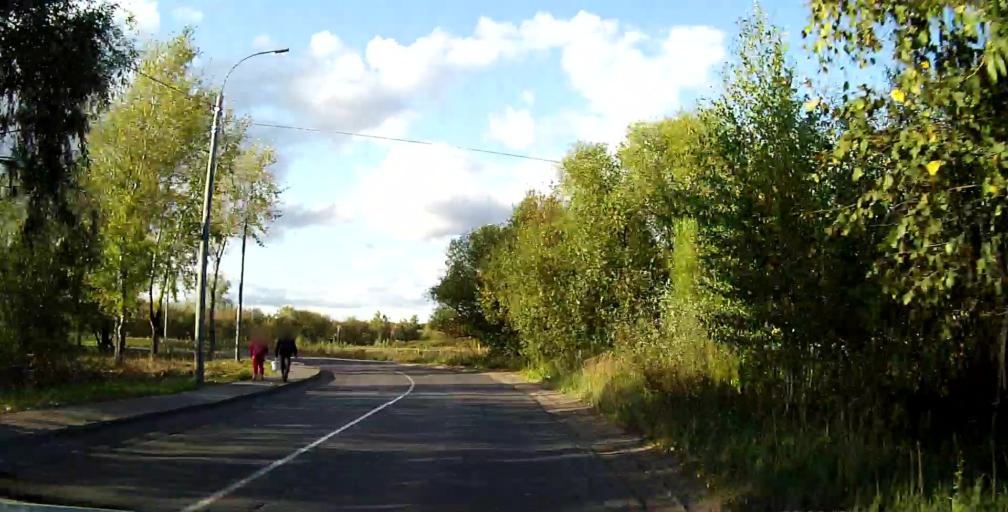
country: RU
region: Moskovskaya
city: Klimovsk
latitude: 55.3795
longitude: 37.5622
